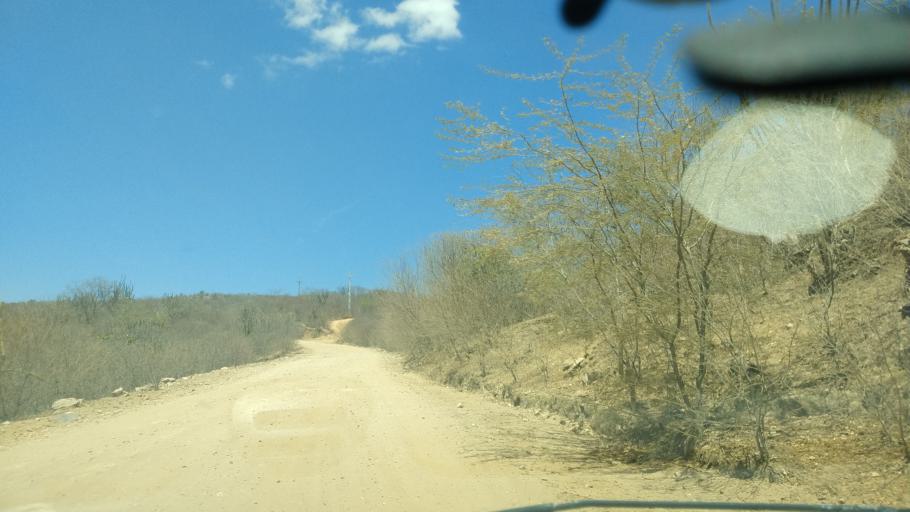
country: BR
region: Rio Grande do Norte
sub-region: Cerro Cora
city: Cerro Cora
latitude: -6.0156
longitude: -36.3143
